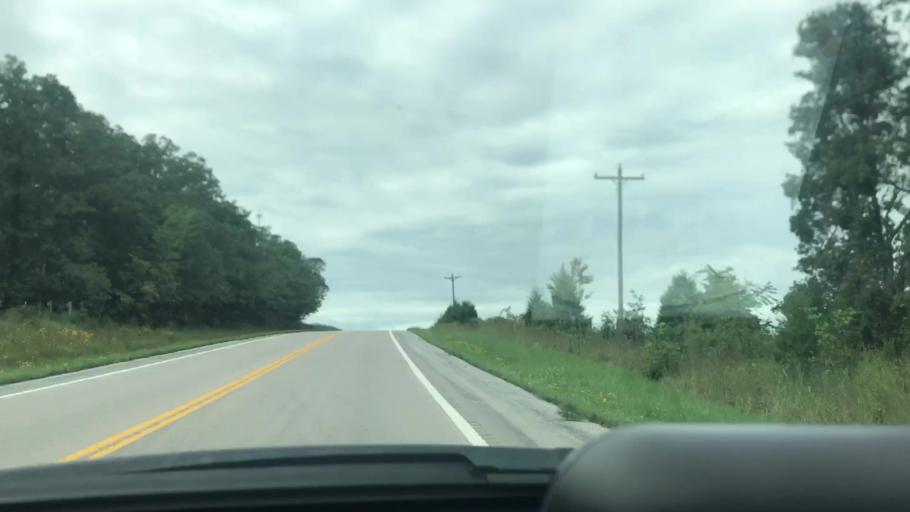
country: US
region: Missouri
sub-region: Benton County
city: Warsaw
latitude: 38.1425
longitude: -93.2884
